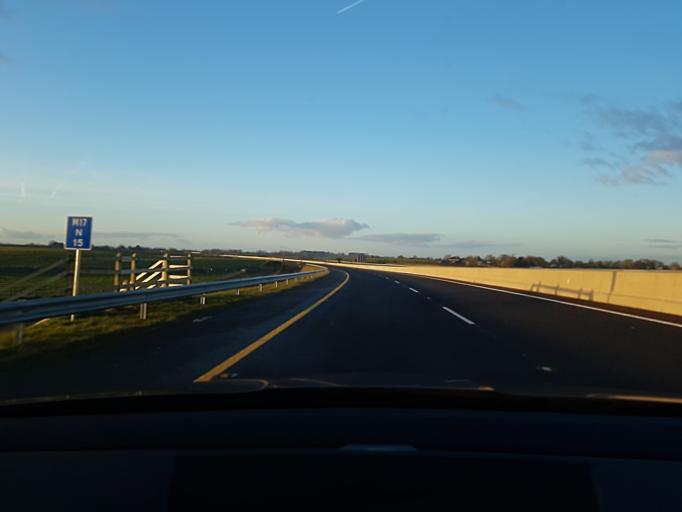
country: IE
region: Connaught
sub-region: County Galway
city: Tuam
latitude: 53.4219
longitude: -8.8302
